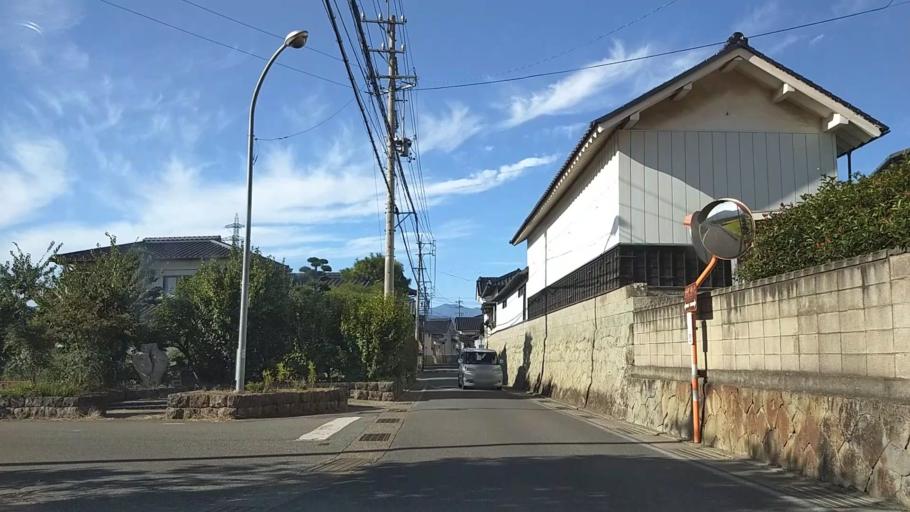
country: JP
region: Nagano
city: Nagano-shi
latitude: 36.5516
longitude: 138.1564
